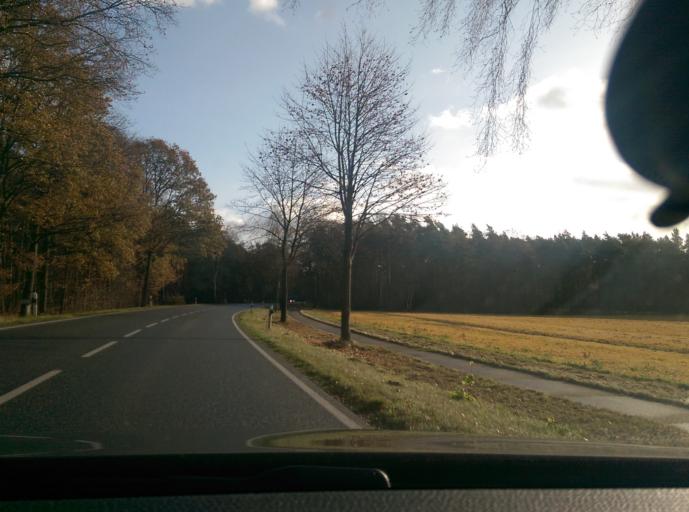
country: DE
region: Lower Saxony
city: Lindwedel
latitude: 52.6679
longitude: 9.7341
